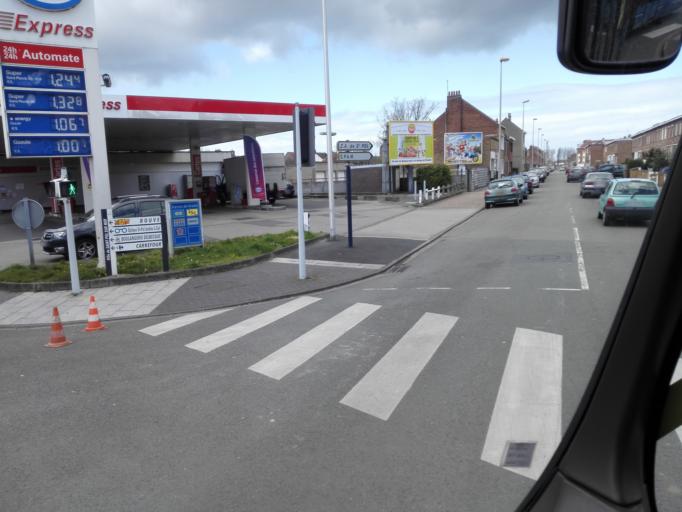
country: FR
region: Nord-Pas-de-Calais
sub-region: Departement du Nord
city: Dunkerque
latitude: 51.0288
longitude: 2.3590
